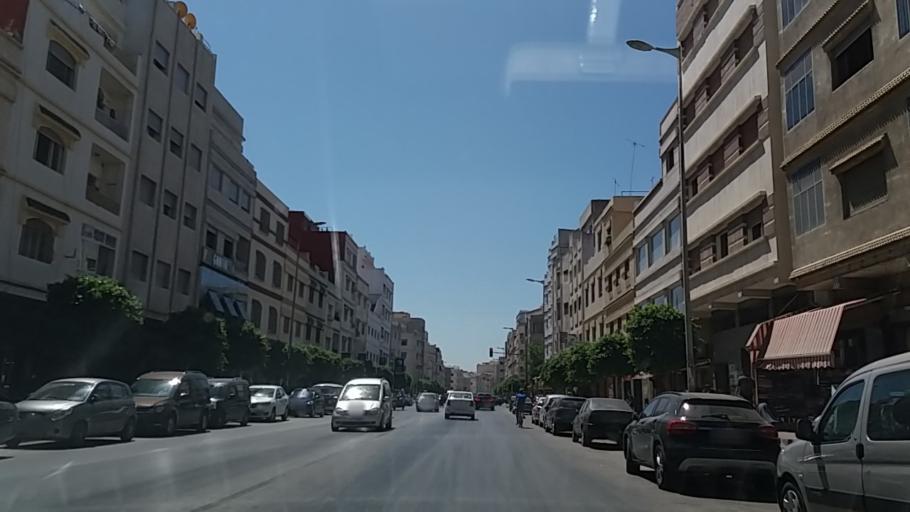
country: MA
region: Tanger-Tetouan
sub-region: Tanger-Assilah
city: Tangier
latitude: 35.7610
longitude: -5.8027
